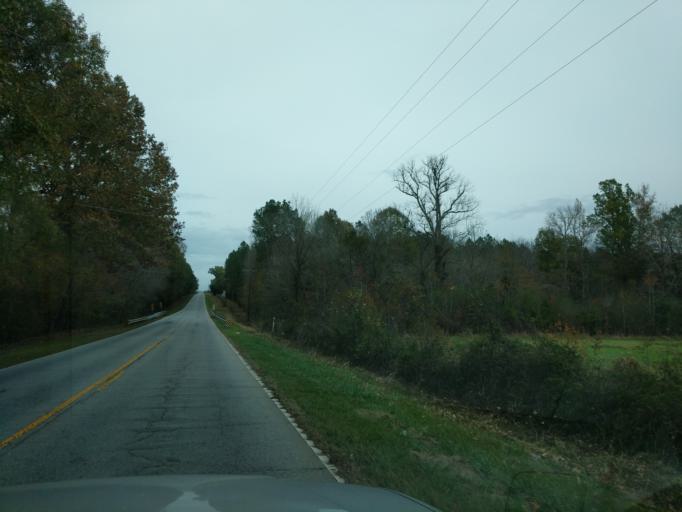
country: US
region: South Carolina
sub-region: Saluda County
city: Saluda
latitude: 34.0917
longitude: -81.7549
